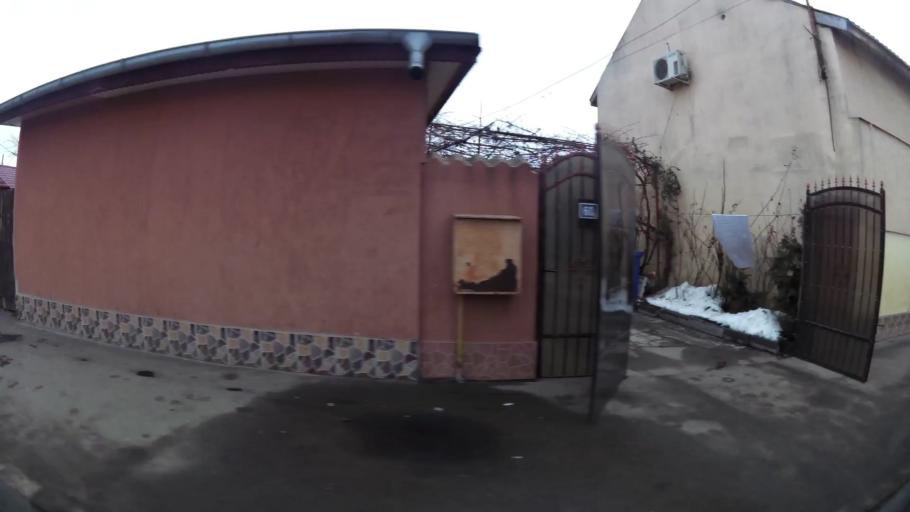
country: RO
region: Ilfov
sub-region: Comuna Pantelimon
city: Pantelimon
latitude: 44.4541
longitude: 26.1960
